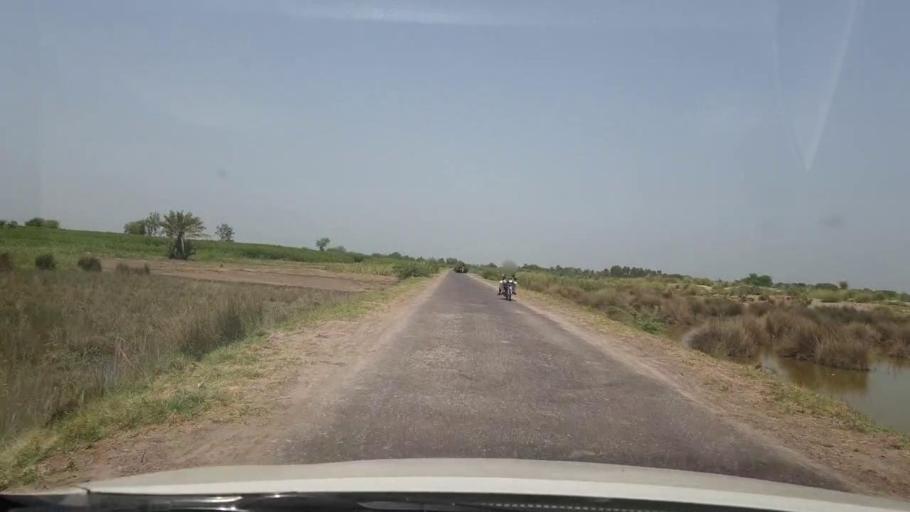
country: PK
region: Sindh
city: Bozdar
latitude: 27.2529
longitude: 68.6404
